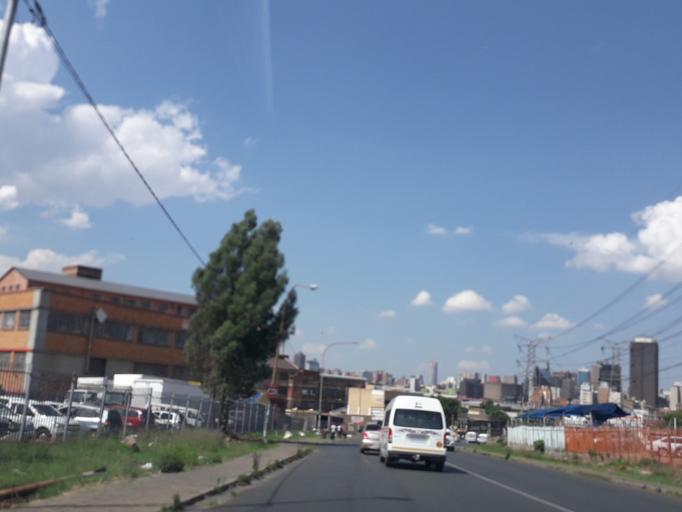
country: ZA
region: Gauteng
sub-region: City of Johannesburg Metropolitan Municipality
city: Johannesburg
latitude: -26.2096
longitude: 28.0218
